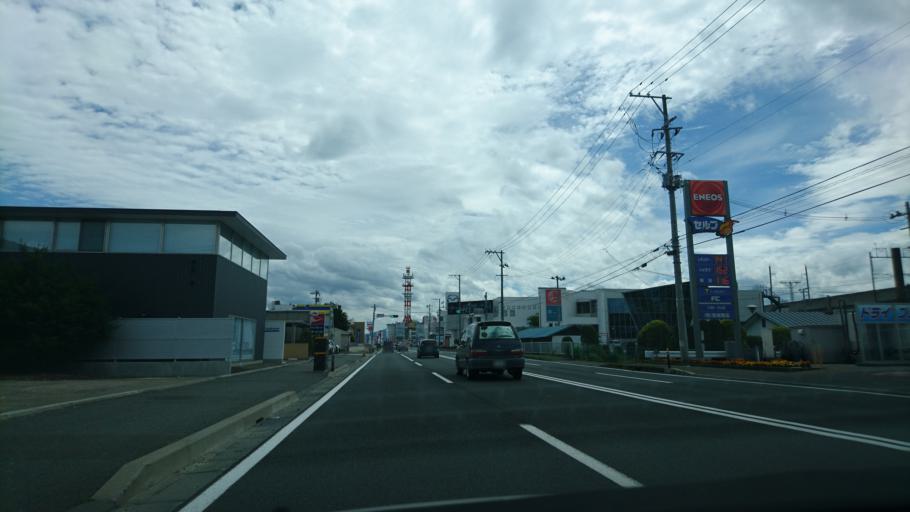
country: JP
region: Iwate
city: Morioka-shi
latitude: 39.7346
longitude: 141.1246
